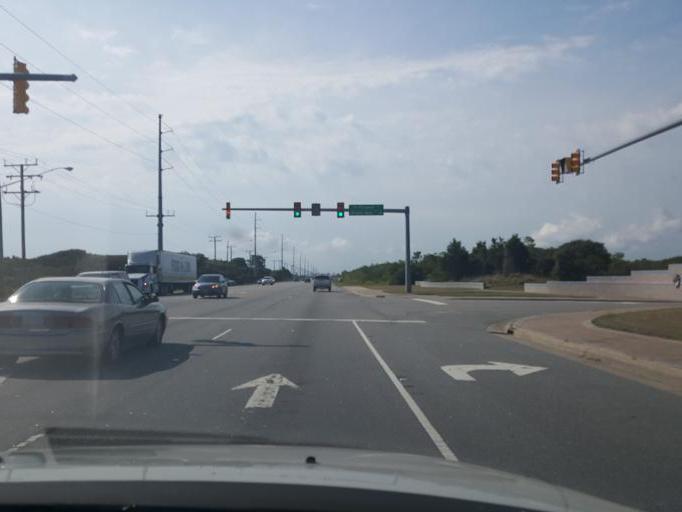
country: US
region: North Carolina
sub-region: Dare County
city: Kill Devil Hills
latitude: 36.0205
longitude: -75.6652
